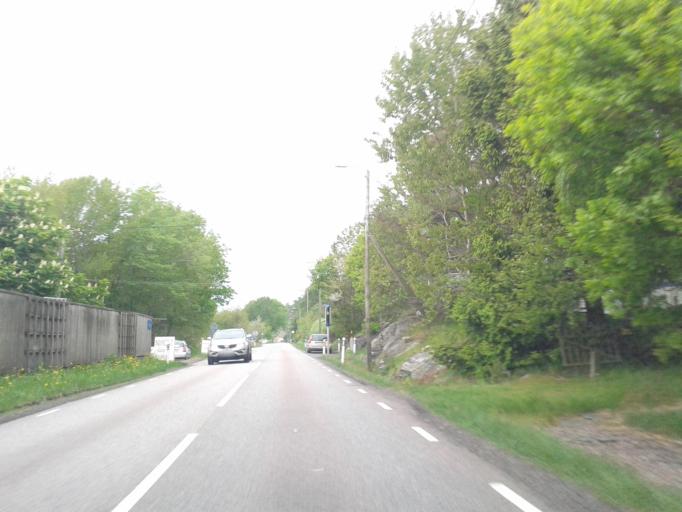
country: SE
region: Vaestra Goetaland
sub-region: Kungalvs Kommun
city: Kode
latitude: 57.8980
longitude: 11.7300
